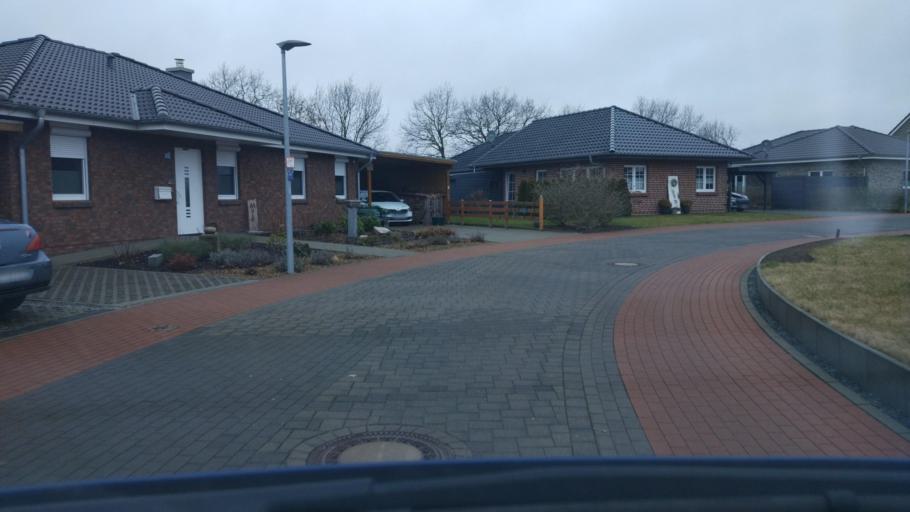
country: DE
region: Schleswig-Holstein
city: Kropp
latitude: 54.4177
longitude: 9.4960
